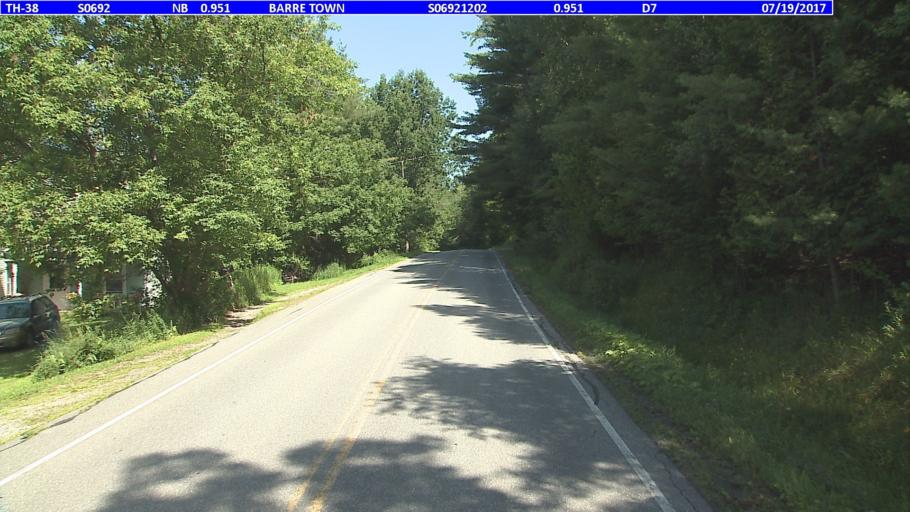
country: US
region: Vermont
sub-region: Washington County
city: South Barre
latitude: 44.1718
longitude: -72.4564
